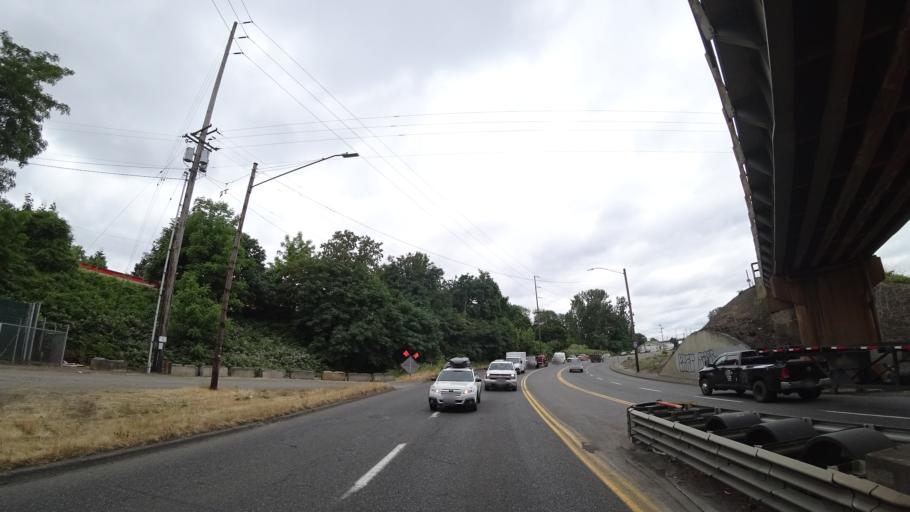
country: US
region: Washington
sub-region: Clark County
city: Vancouver
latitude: 45.5840
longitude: -122.6798
